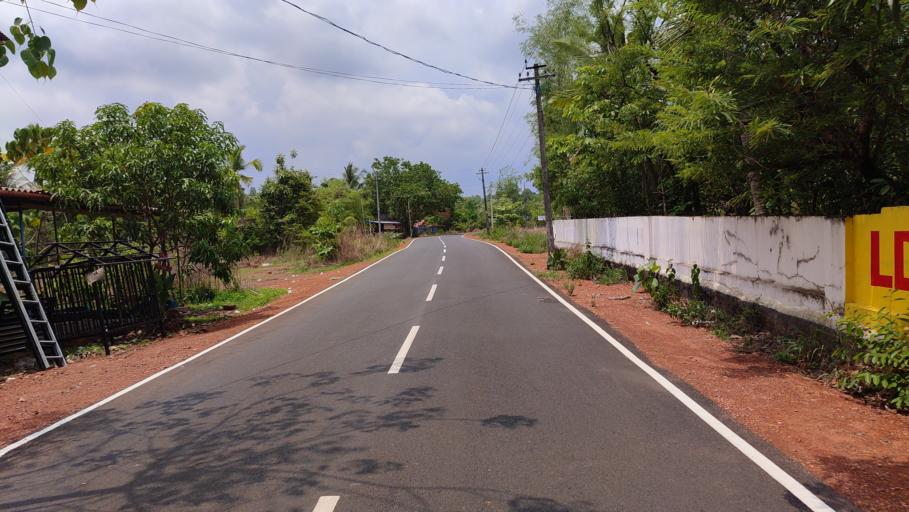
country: IN
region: Kerala
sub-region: Kasaragod District
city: Kannangad
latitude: 12.3208
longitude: 75.1237
